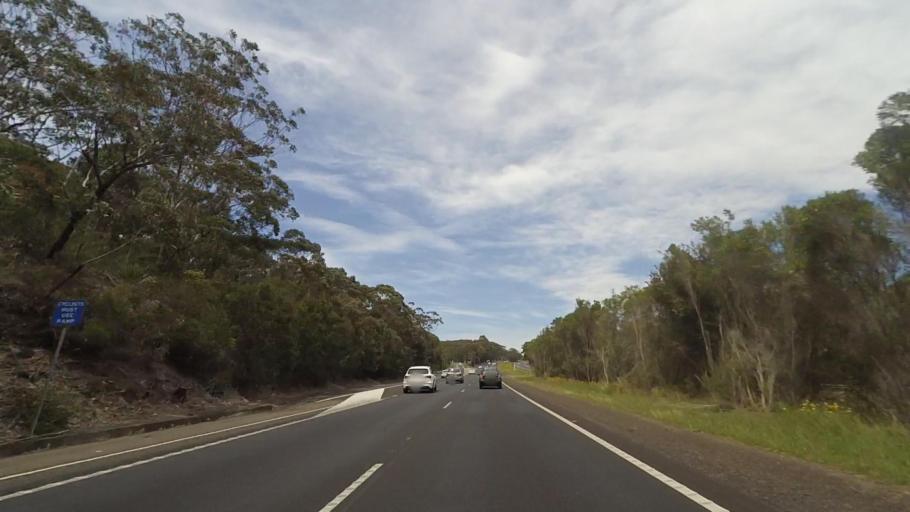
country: AU
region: New South Wales
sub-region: Wollongong
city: Helensburgh
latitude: -34.1982
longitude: 150.9661
